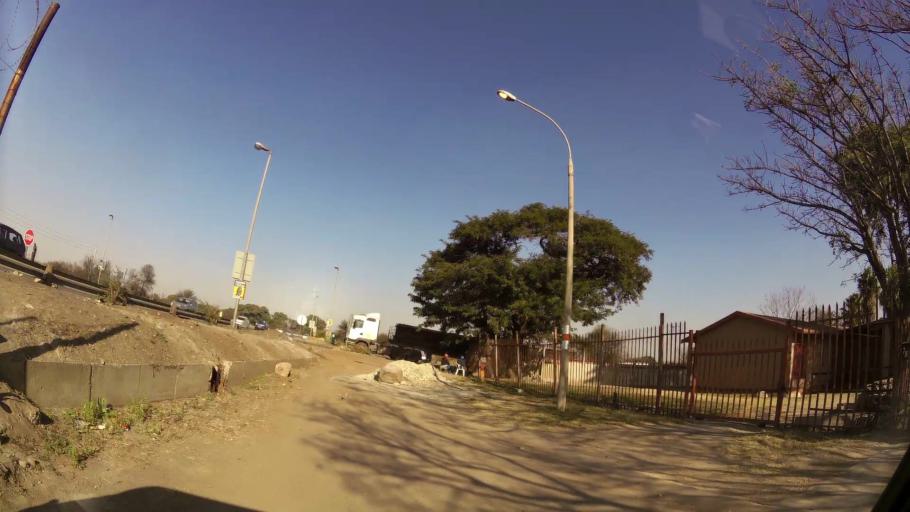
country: ZA
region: North-West
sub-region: Bojanala Platinum District Municipality
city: Rustenburg
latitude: -25.6596
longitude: 27.2663
